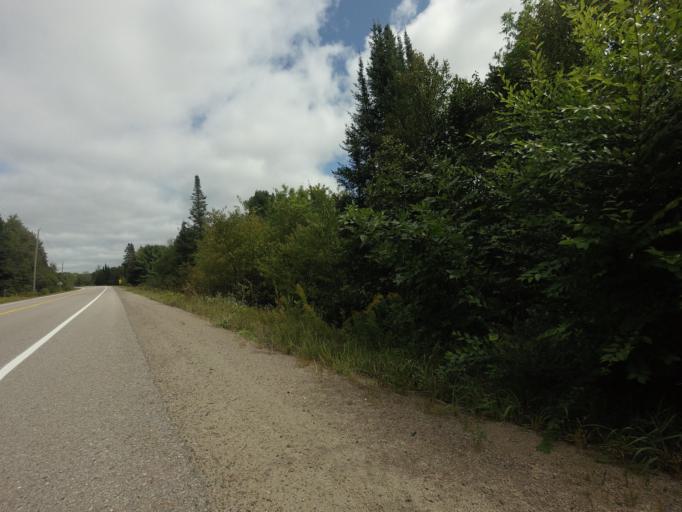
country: CA
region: Ontario
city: Omemee
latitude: 44.8946
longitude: -78.4664
